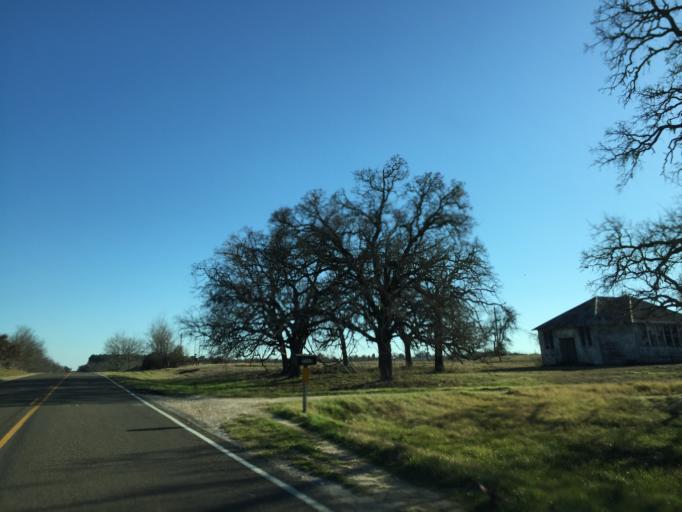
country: US
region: Texas
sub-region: Bastrop County
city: Elgin
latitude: 30.4077
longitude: -97.2526
